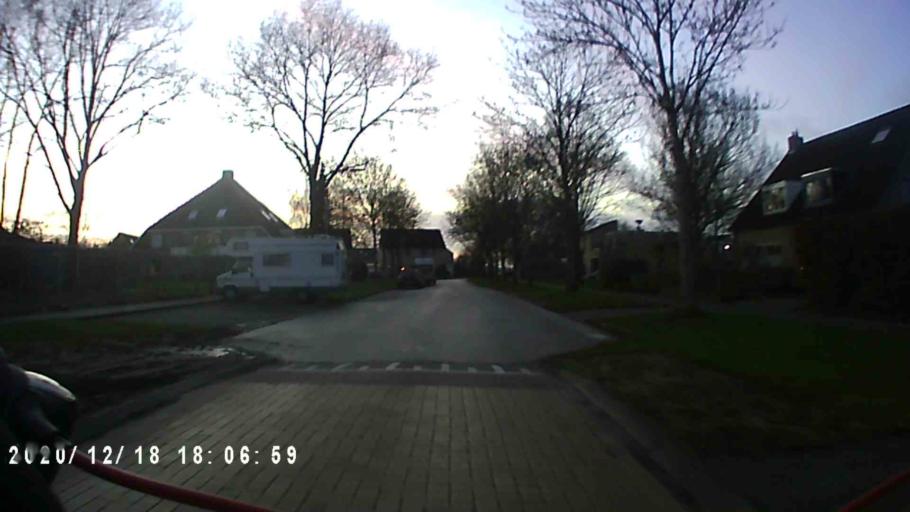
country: NL
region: Groningen
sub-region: Gemeente Haren
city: Haren
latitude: 53.1364
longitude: 6.5562
